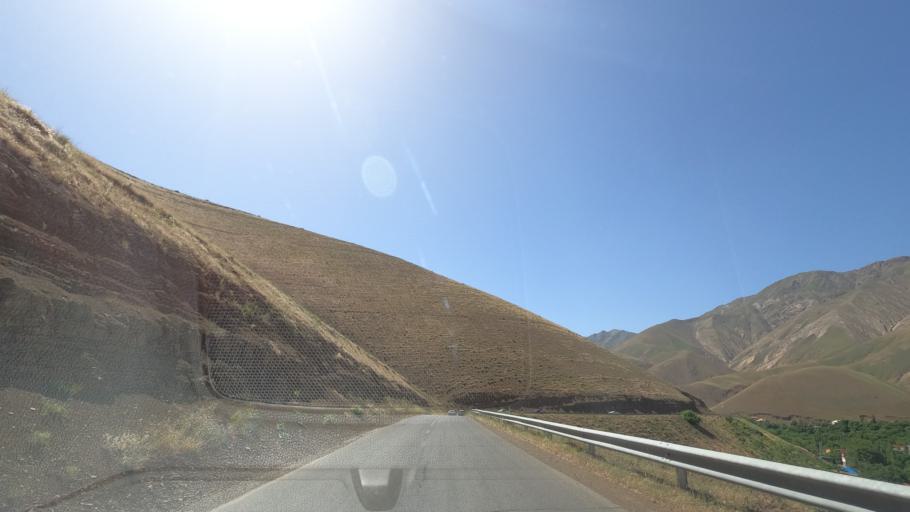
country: IR
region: Alborz
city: Karaj
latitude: 35.9287
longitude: 51.0860
